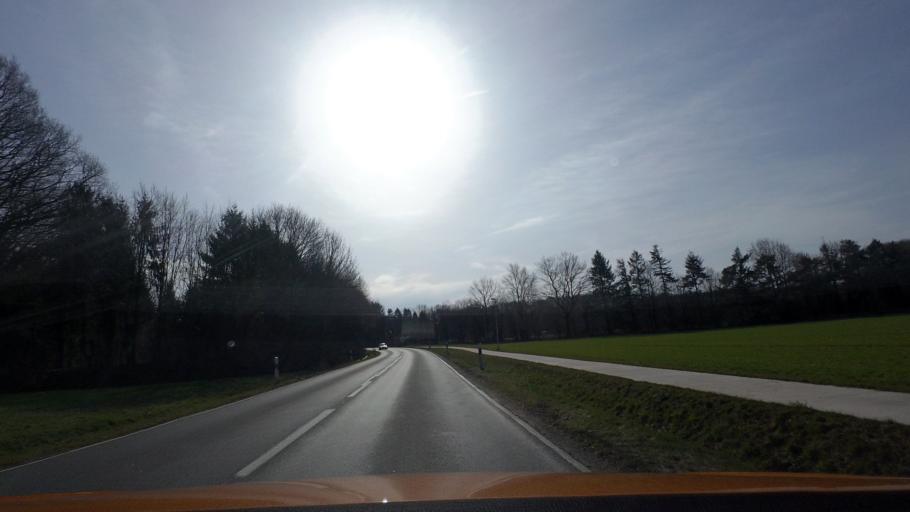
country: DE
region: Lower Saxony
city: Wiedensahl
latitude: 52.3729
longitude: 9.1268
